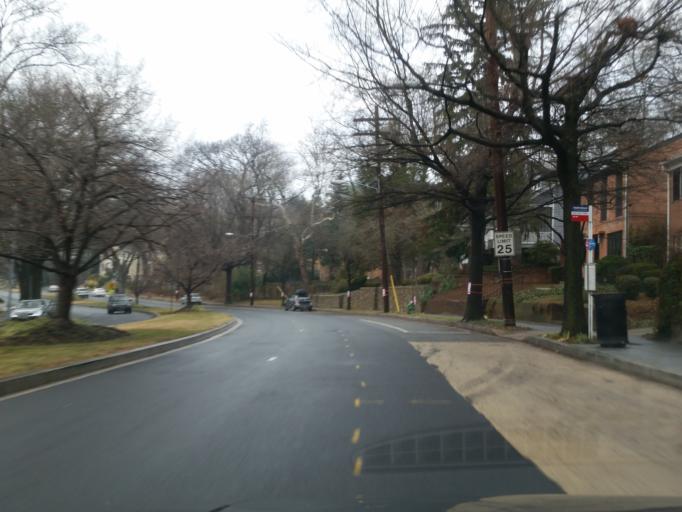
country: US
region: Maryland
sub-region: Montgomery County
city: Brookmont
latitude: 38.9304
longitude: -77.1068
